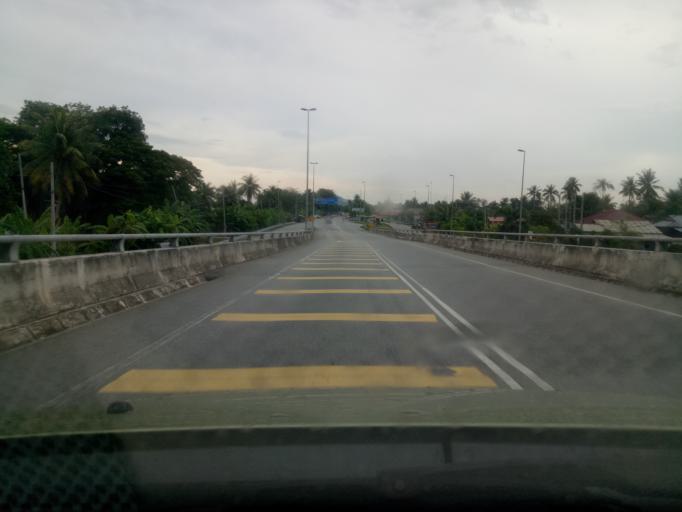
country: MY
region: Kedah
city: Gurun
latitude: 5.9710
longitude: 100.4394
